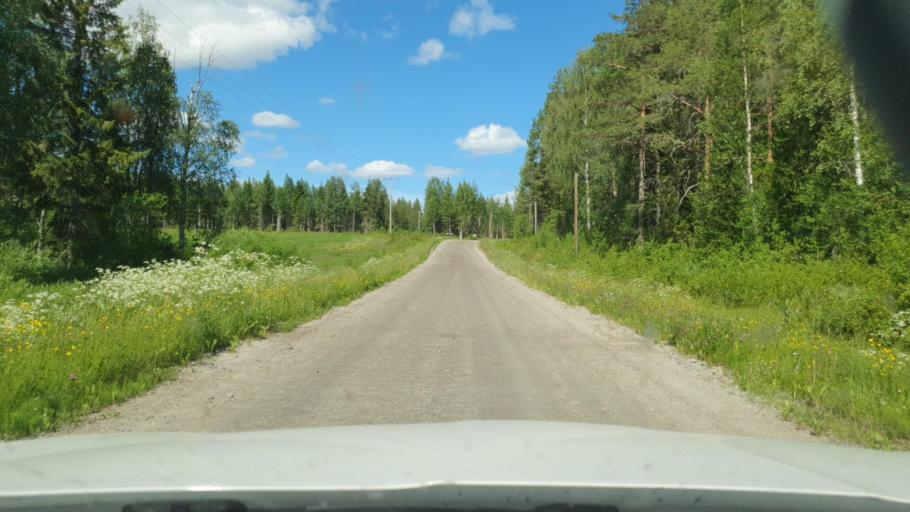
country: SE
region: Vaesterbotten
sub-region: Skelleftea Kommun
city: Backa
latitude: 65.1520
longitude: 21.1619
